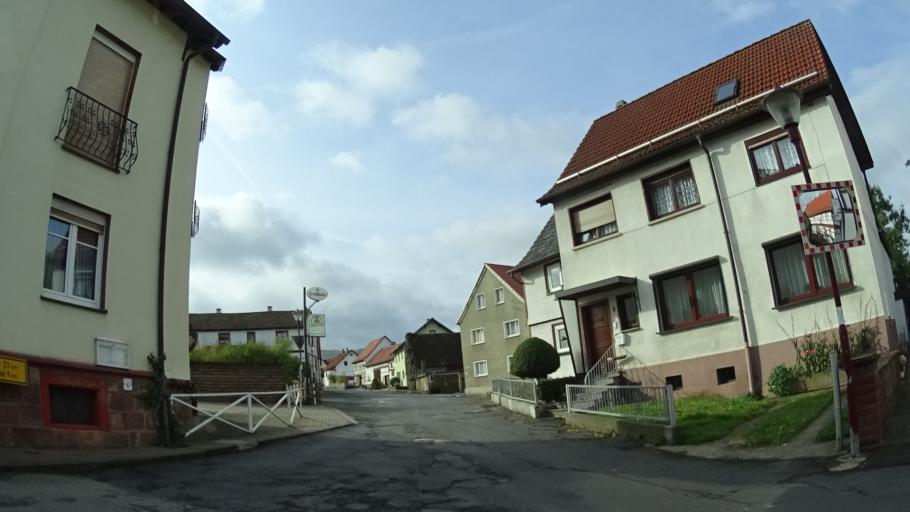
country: DE
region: Thuringia
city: Oberweid
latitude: 50.5907
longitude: 10.0639
